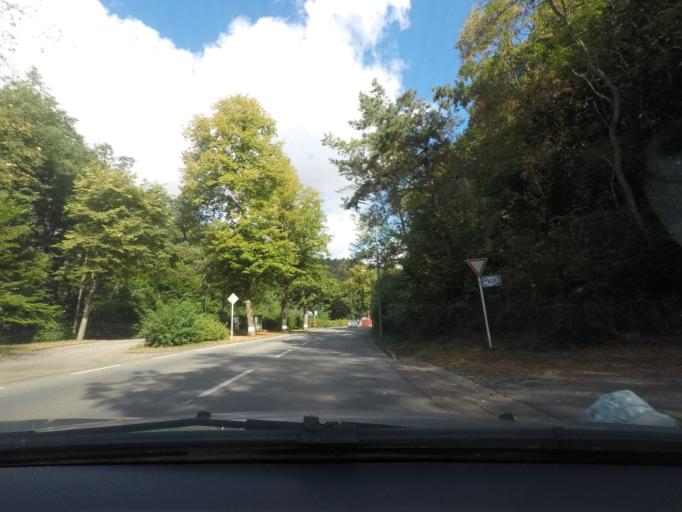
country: LU
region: Luxembourg
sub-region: Canton de Mersch
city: Heffingen
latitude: 49.7426
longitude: 6.2664
